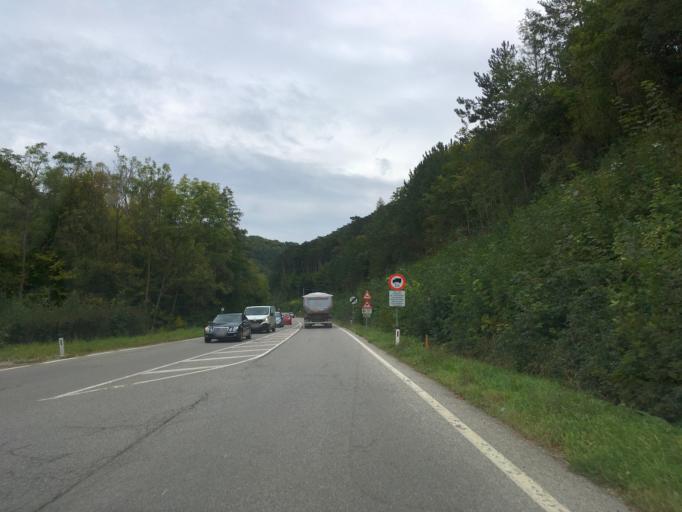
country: AT
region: Lower Austria
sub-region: Politischer Bezirk Modling
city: Gaaden
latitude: 48.0683
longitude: 16.2166
